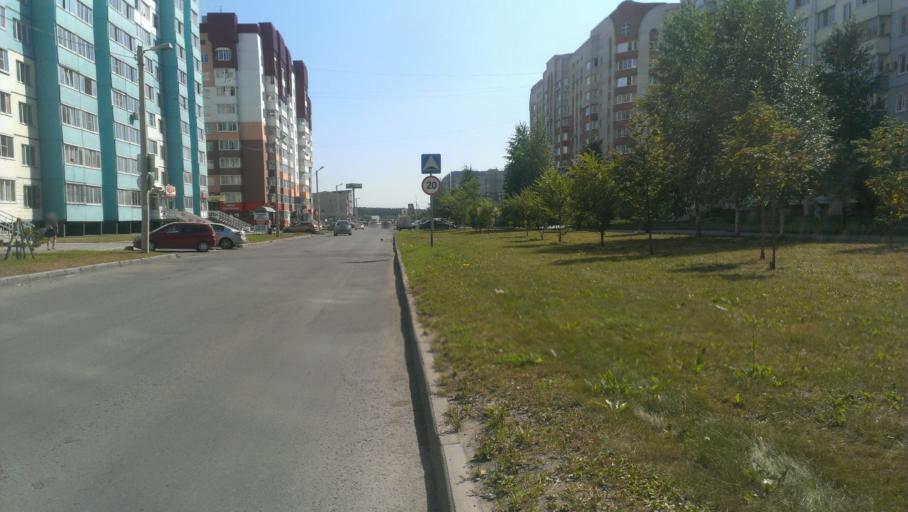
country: RU
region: Altai Krai
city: Novosilikatnyy
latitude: 53.3321
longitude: 83.6848
